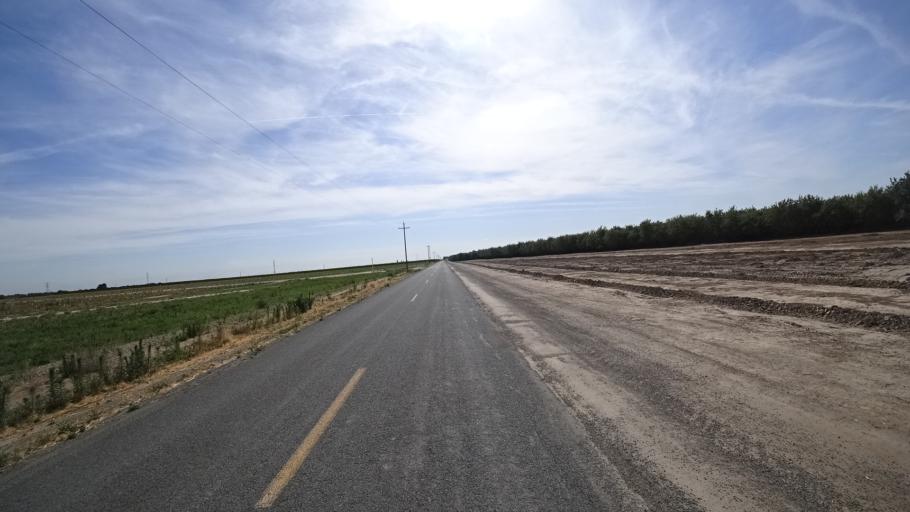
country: US
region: California
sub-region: Kings County
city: Lucerne
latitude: 36.4158
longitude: -119.5977
